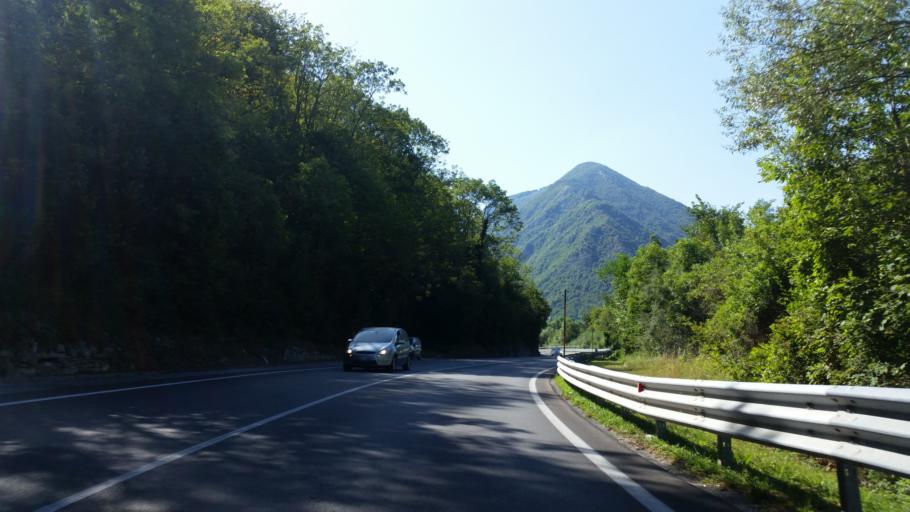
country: IT
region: Piedmont
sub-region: Provincia di Cuneo
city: Vernante
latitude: 44.2528
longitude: 7.5297
